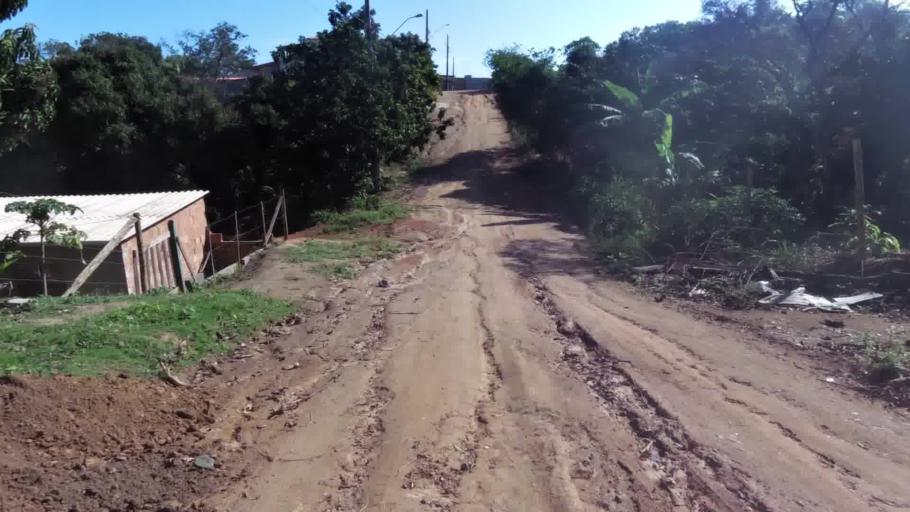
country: BR
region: Espirito Santo
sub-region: Piuma
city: Piuma
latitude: -20.8252
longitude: -40.6229
